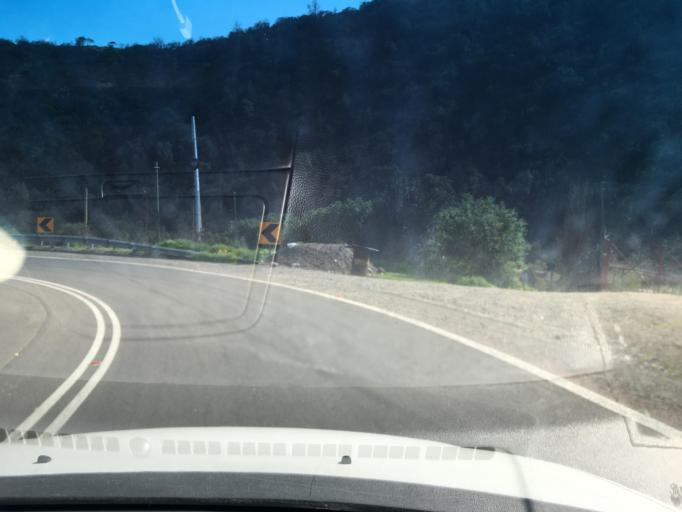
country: CL
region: Valparaiso
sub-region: Provincia de Marga Marga
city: Limache
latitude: -33.0581
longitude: -71.0455
